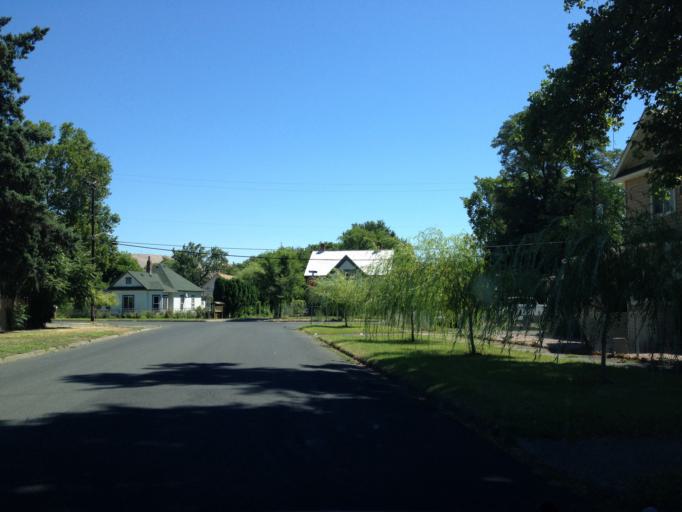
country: US
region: Washington
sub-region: Yakima County
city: Yakima
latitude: 46.6021
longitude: -120.4944
